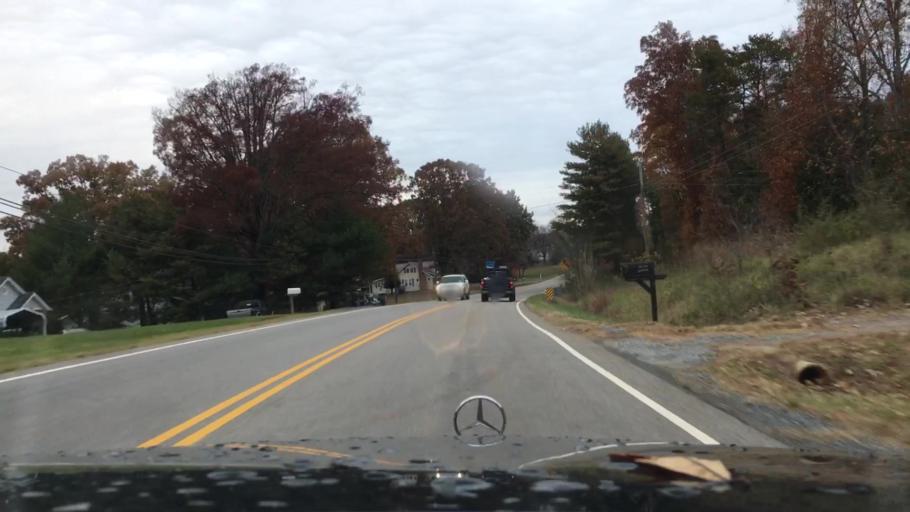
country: US
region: Virginia
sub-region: Campbell County
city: Altavista
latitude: 37.1362
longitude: -79.3068
